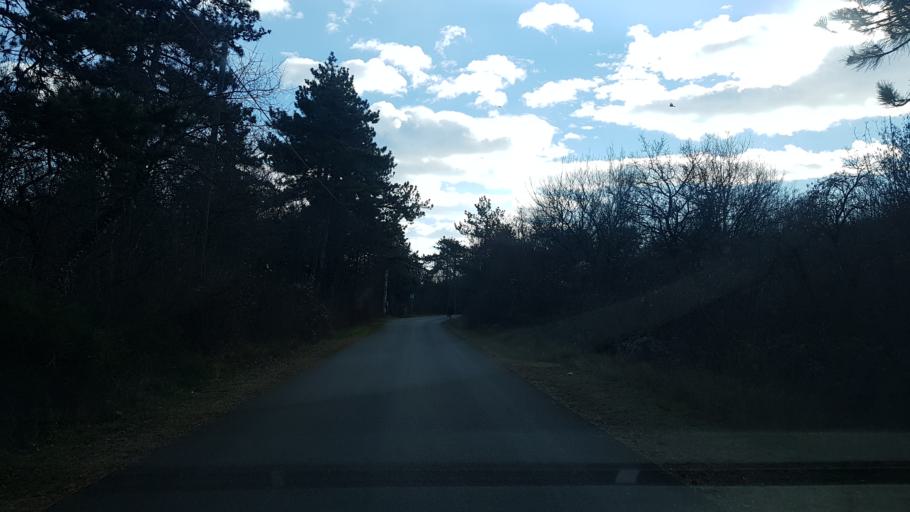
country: IT
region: Friuli Venezia Giulia
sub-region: Provincia di Gorizia
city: Gradisca d'Isonzo
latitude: 45.8811
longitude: 13.5230
